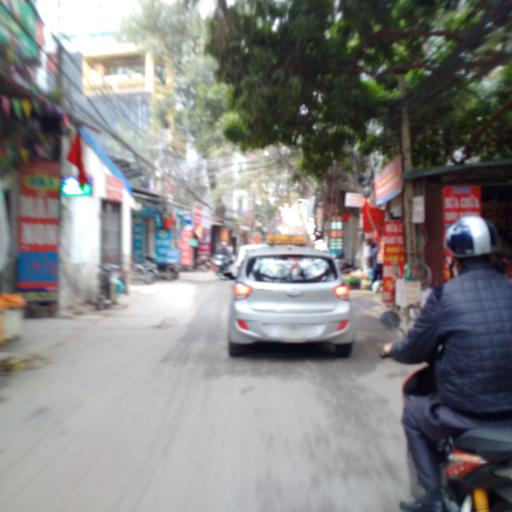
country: VN
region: Ha Noi
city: Cau Dien
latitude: 21.0683
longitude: 105.7786
